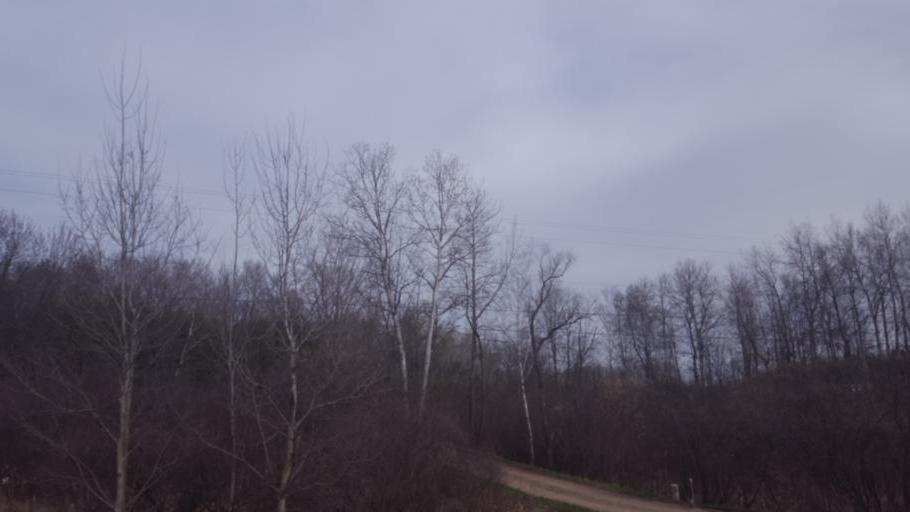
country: US
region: Michigan
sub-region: Clare County
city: Clare
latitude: 43.8693
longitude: -84.7680
